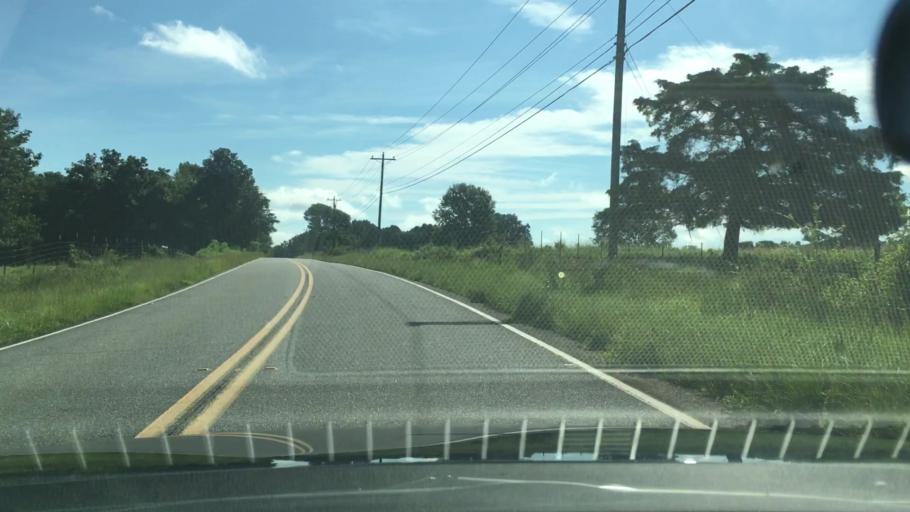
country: US
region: Georgia
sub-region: Putnam County
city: Jefferson
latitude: 33.4386
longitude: -83.3528
